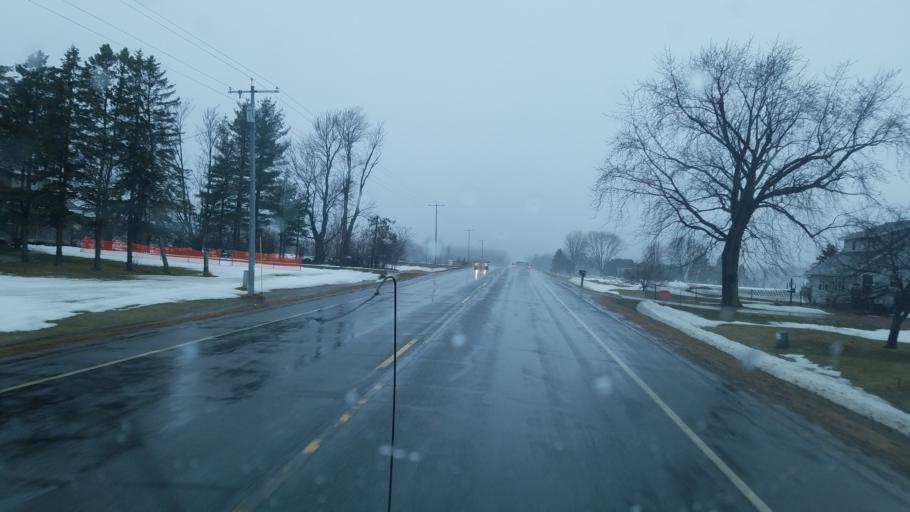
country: US
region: Wisconsin
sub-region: Wood County
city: Marshfield
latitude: 44.6778
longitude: -90.2398
